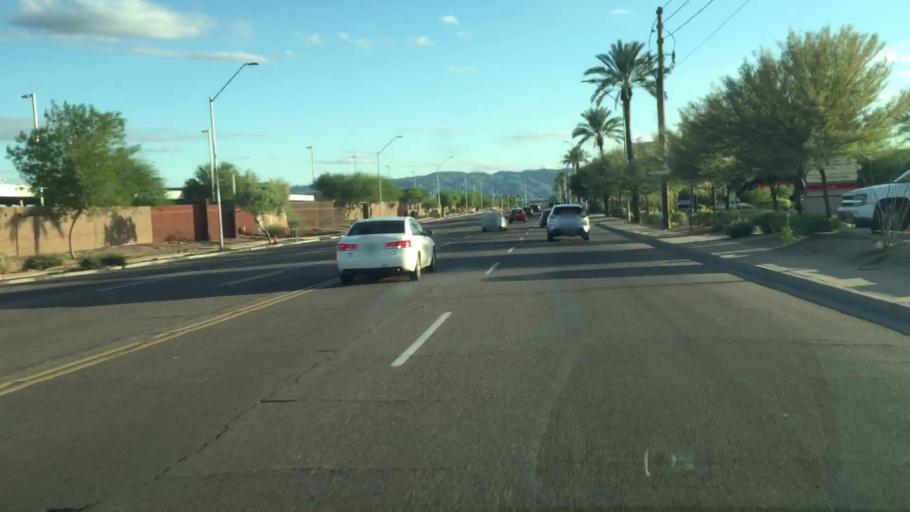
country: US
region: Arizona
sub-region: Maricopa County
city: Phoenix
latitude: 33.4358
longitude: -112.0479
